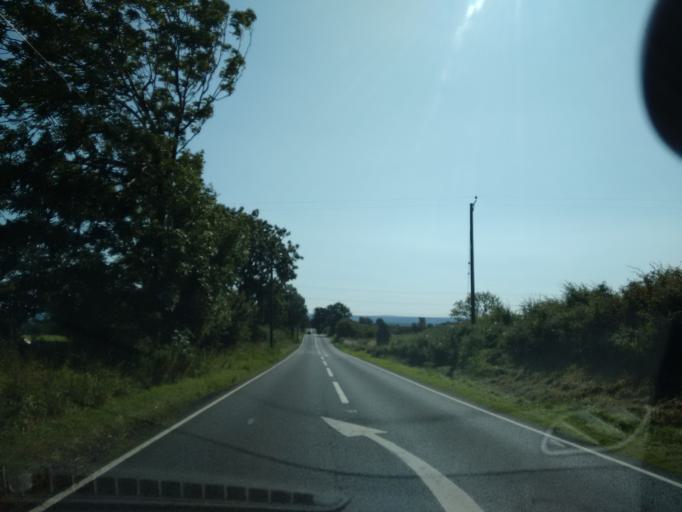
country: GB
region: England
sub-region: Northumberland
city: Corbridge
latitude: 55.0108
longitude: -2.0208
